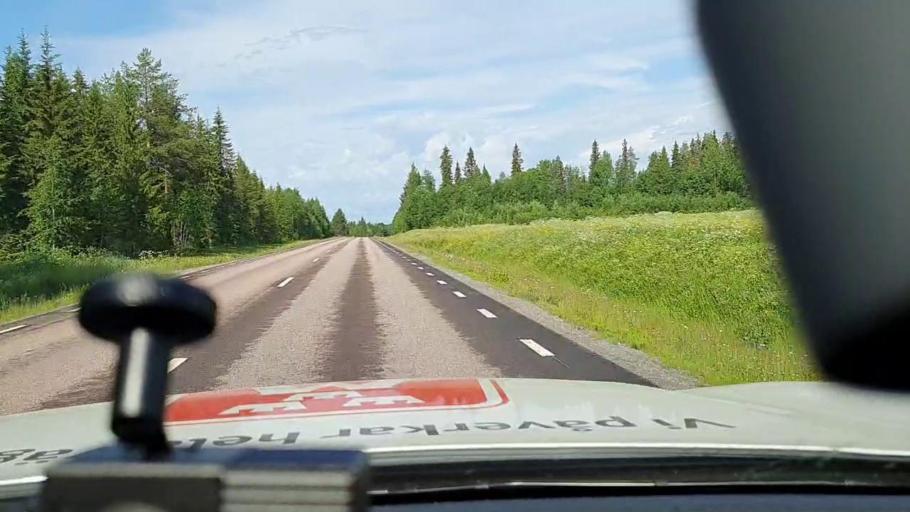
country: SE
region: Norrbotten
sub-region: Alvsbyns Kommun
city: AElvsbyn
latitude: 66.0229
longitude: 21.1248
